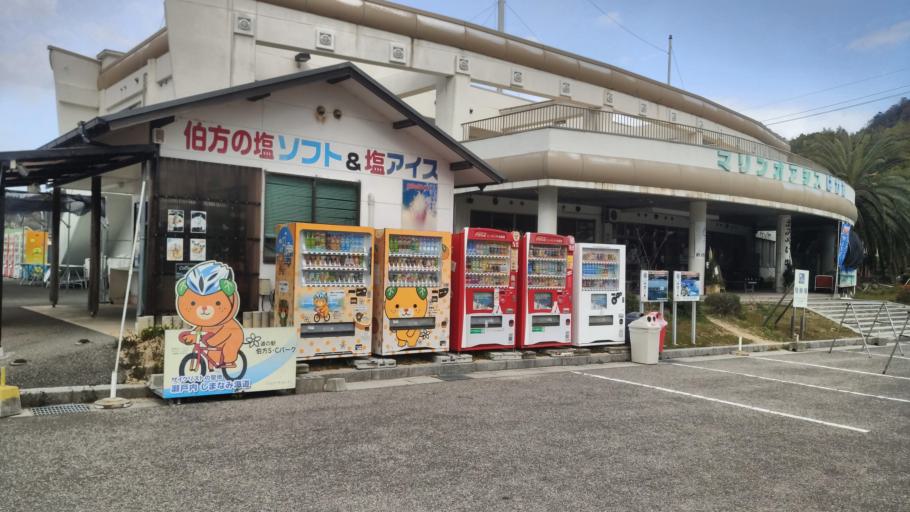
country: JP
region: Hiroshima
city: Innoshima
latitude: 34.2026
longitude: 133.0753
